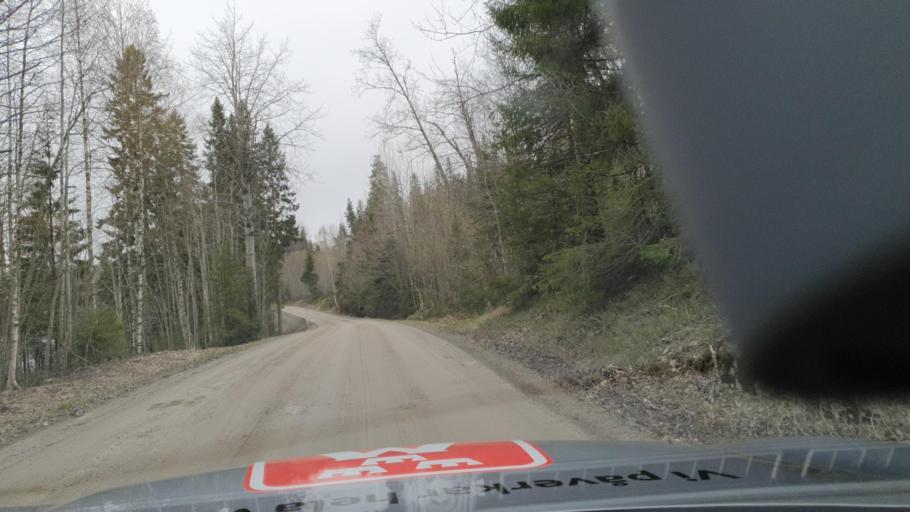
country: SE
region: Vaesternorrland
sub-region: OErnskoeldsviks Kommun
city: Husum
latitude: 63.6361
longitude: 19.0588
